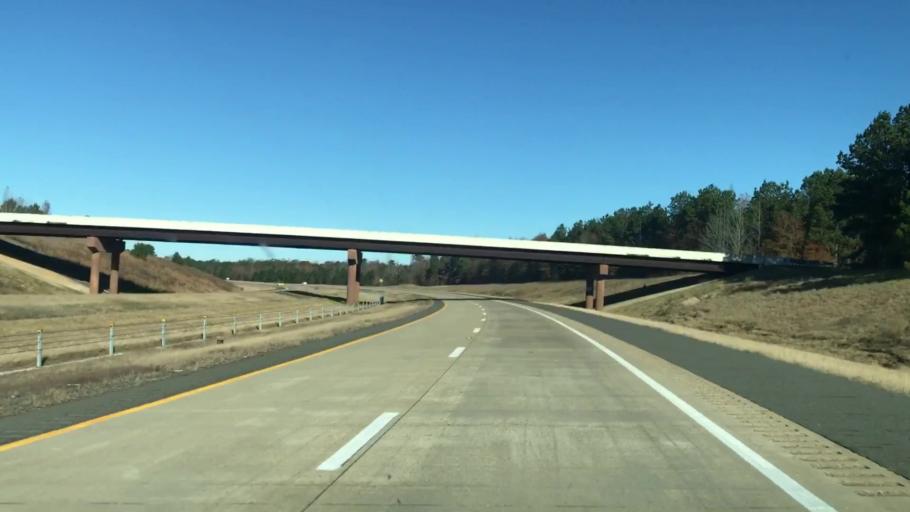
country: US
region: Texas
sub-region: Bowie County
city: Texarkana
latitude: 33.2685
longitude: -93.8977
